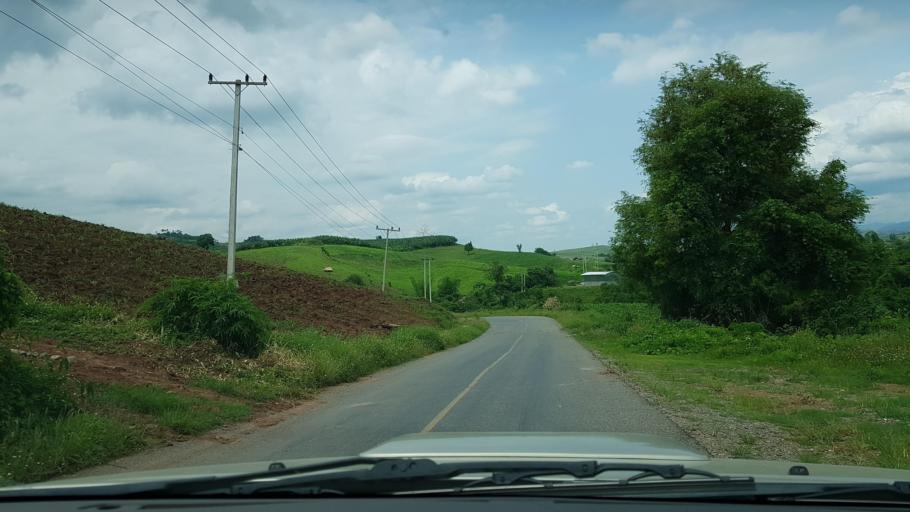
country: TH
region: Nan
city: Chaloem Phra Kiat
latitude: 20.0174
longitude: 101.3205
